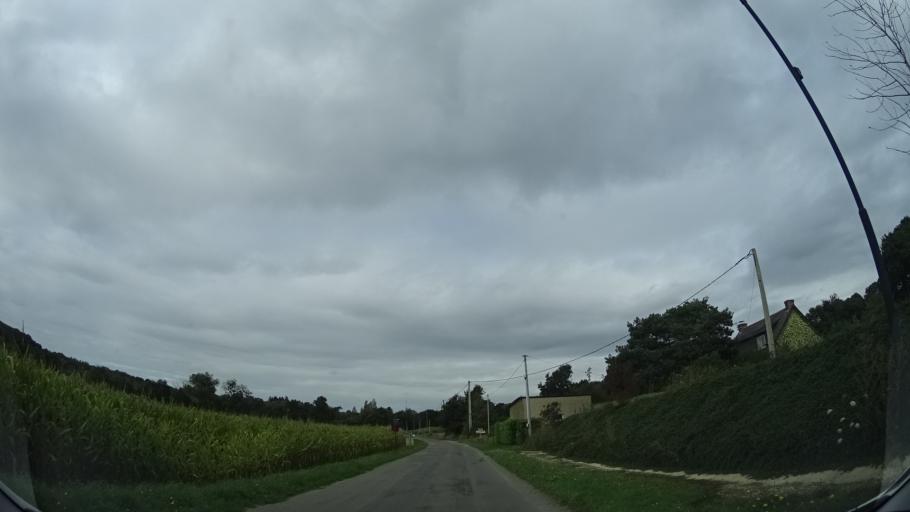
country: FR
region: Brittany
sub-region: Departement d'Ille-et-Vilaine
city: Irodouer
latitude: 48.2844
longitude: -1.8930
